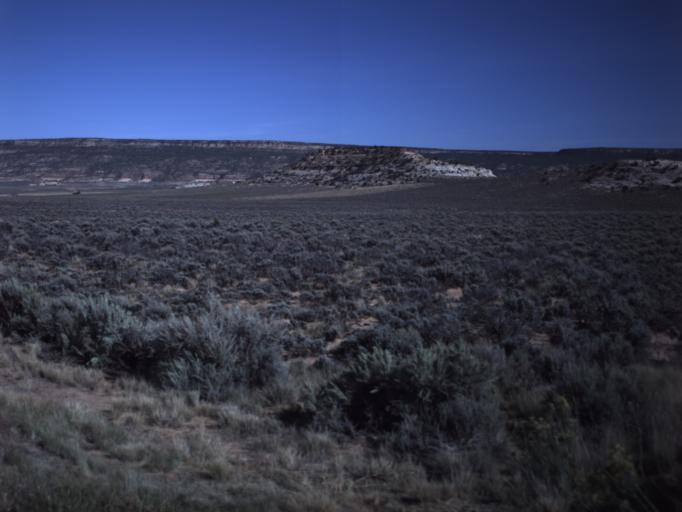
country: US
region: Utah
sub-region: San Juan County
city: Monticello
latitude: 38.0610
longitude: -109.3994
